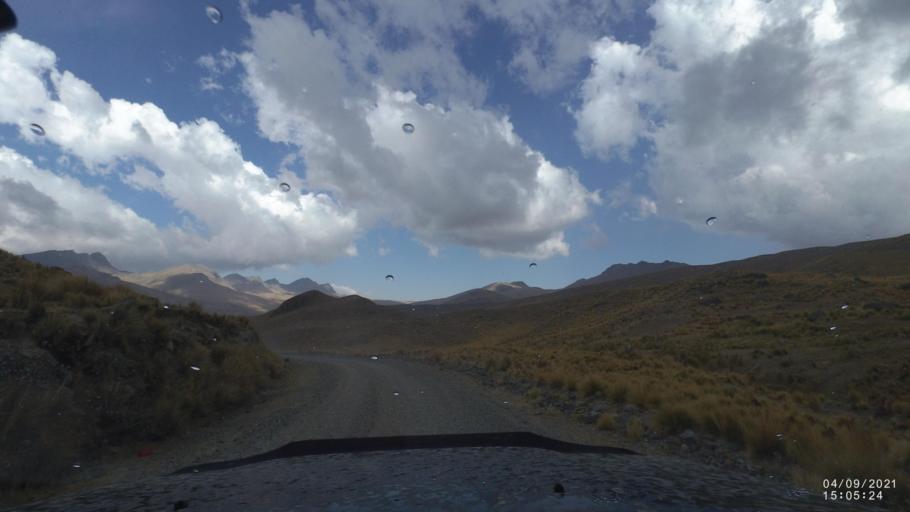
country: BO
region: Cochabamba
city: Sipe Sipe
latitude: -17.1801
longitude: -66.3645
